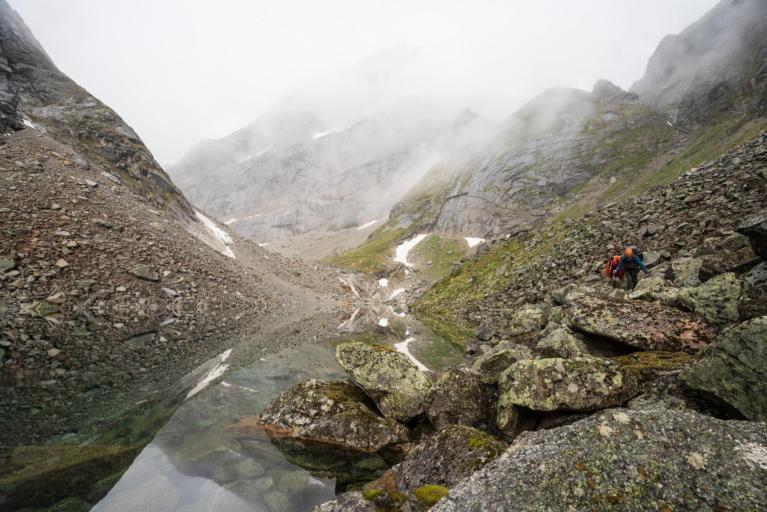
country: RU
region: Transbaikal Territory
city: Chara
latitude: 56.8755
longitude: 117.4010
